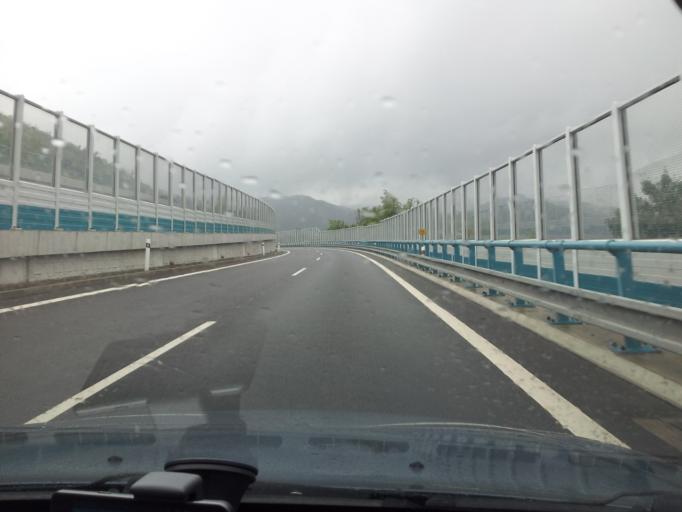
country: SK
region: Banskobystricky
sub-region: Okres Banska Bystrica
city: Banska Bystrica
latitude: 48.7450
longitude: 19.1565
